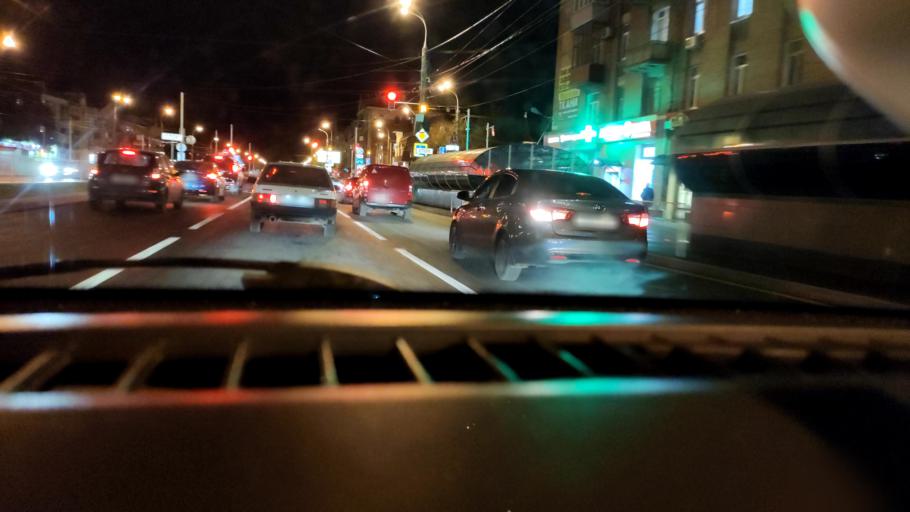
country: RU
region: Samara
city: Samara
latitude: 53.2121
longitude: 50.2471
